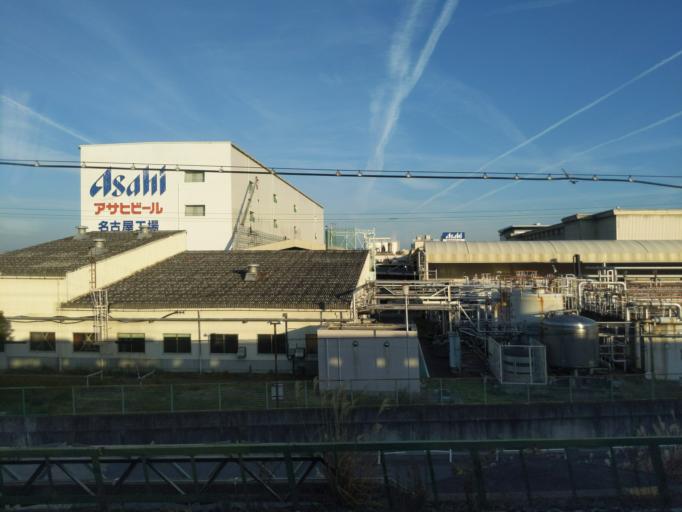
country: JP
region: Aichi
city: Kasugai
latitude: 35.2151
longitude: 136.9535
